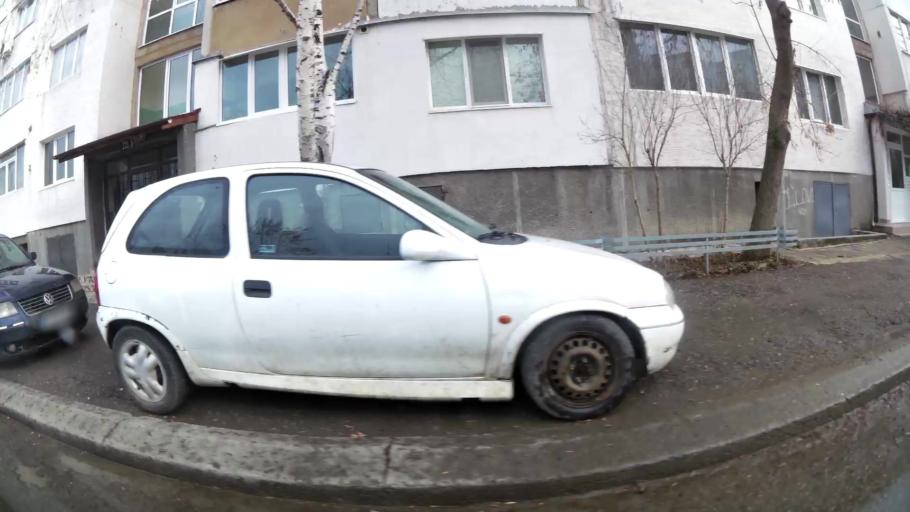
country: BG
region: Sofia-Capital
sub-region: Stolichna Obshtina
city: Sofia
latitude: 42.7467
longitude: 23.2734
